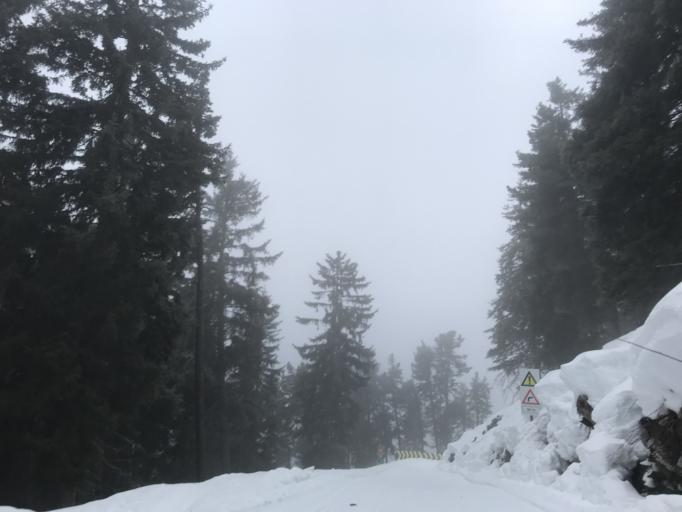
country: IT
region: Trentino-Alto Adige
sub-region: Bolzano
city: San Pietro
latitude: 46.6852
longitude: 11.7017
